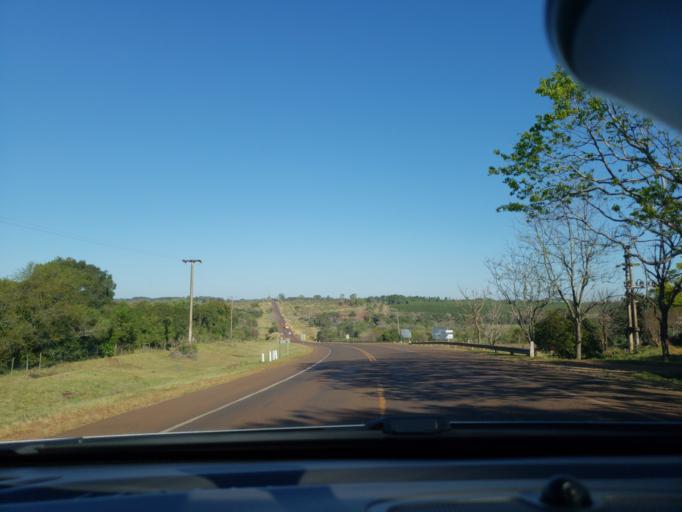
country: AR
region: Misiones
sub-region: Departamento de Apostoles
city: San Jose
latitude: -27.7742
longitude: -55.7734
